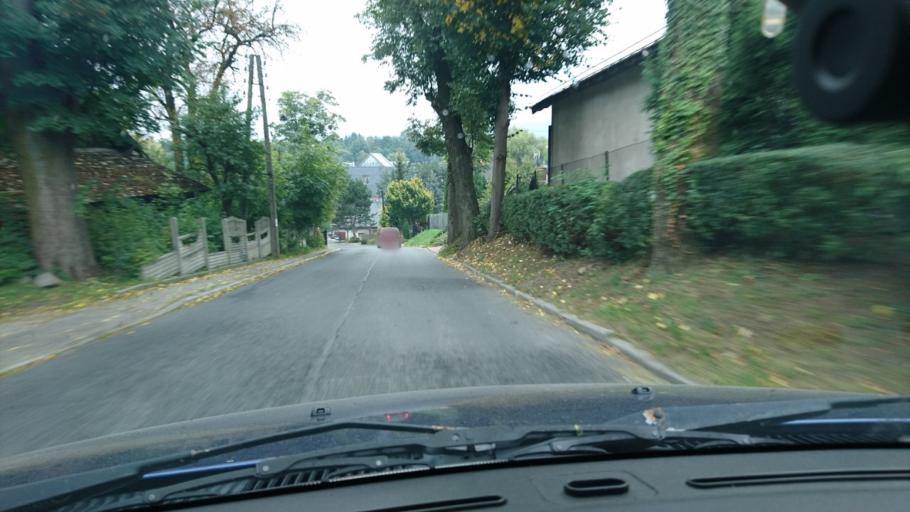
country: PL
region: Silesian Voivodeship
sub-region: Bielsko-Biala
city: Bielsko-Biala
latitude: 49.8264
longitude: 19.0110
